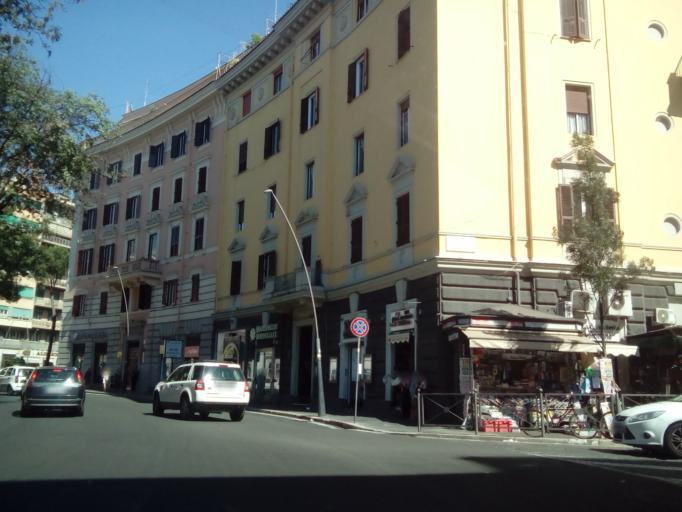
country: IT
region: Latium
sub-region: Citta metropolitana di Roma Capitale
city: Rome
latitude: 41.8813
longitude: 12.5136
